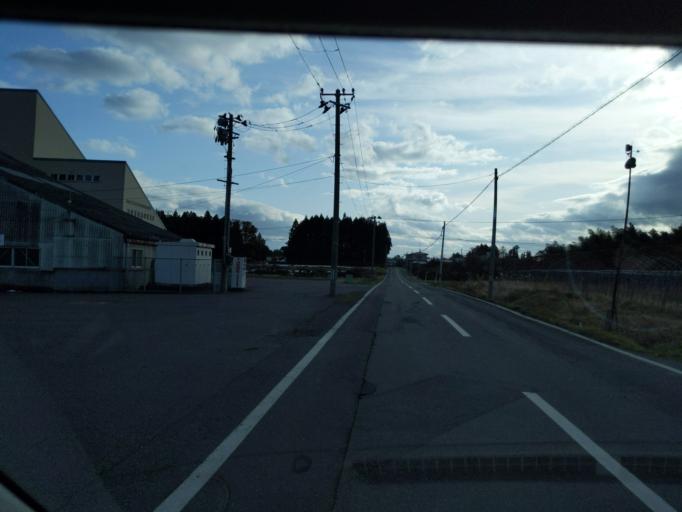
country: JP
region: Iwate
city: Mizusawa
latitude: 39.1049
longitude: 141.0815
